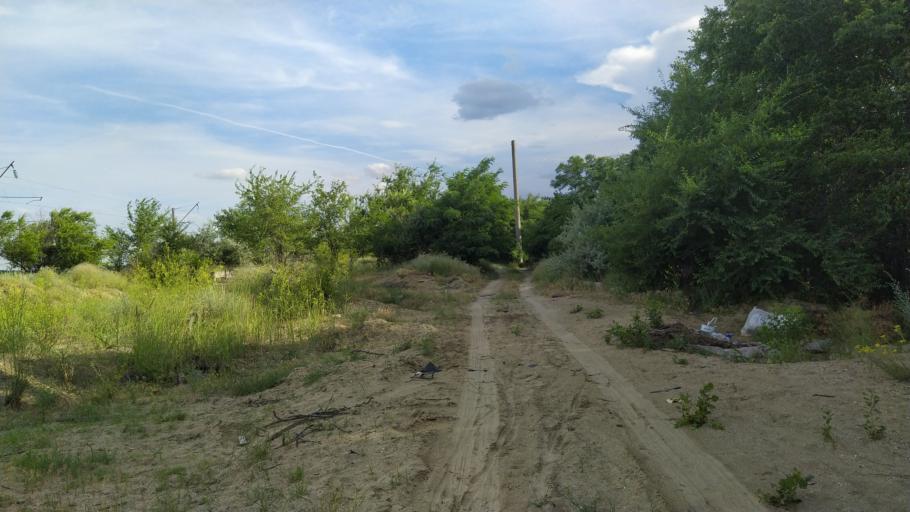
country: RU
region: Rostov
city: Bataysk
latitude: 47.1188
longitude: 39.7130
